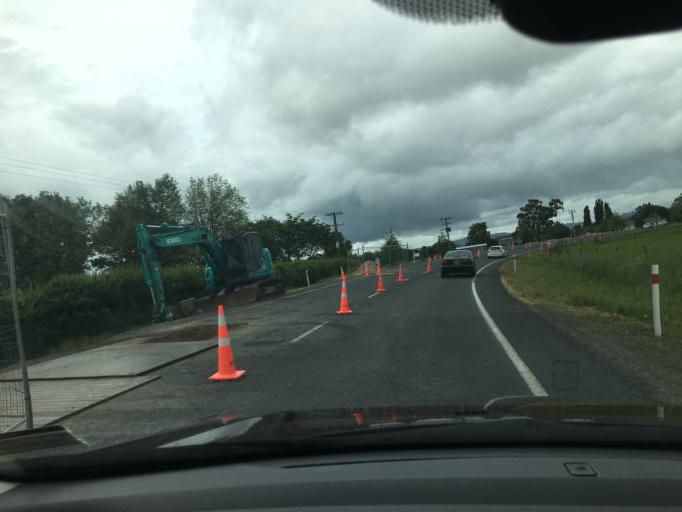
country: NZ
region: Waikato
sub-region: Waipa District
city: Cambridge
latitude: -37.9197
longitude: 175.4377
